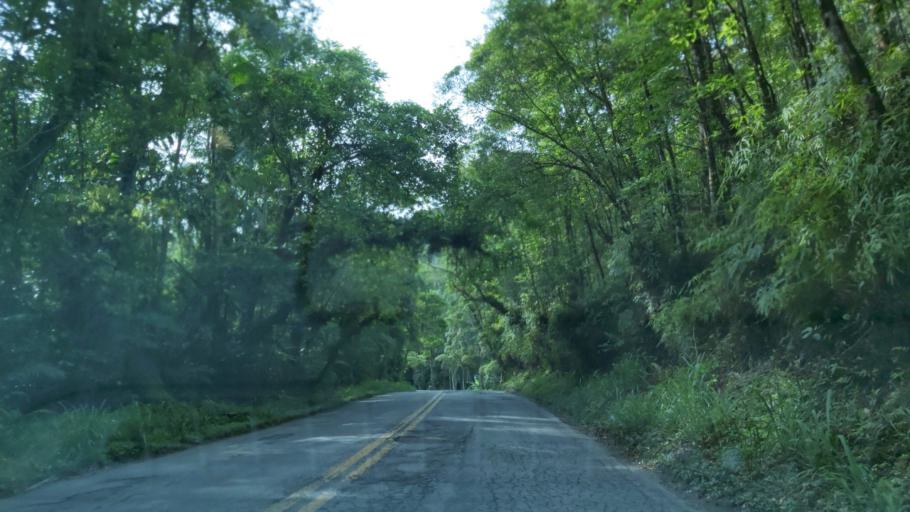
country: BR
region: Sao Paulo
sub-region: Miracatu
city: Miracatu
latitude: -24.0575
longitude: -47.5779
